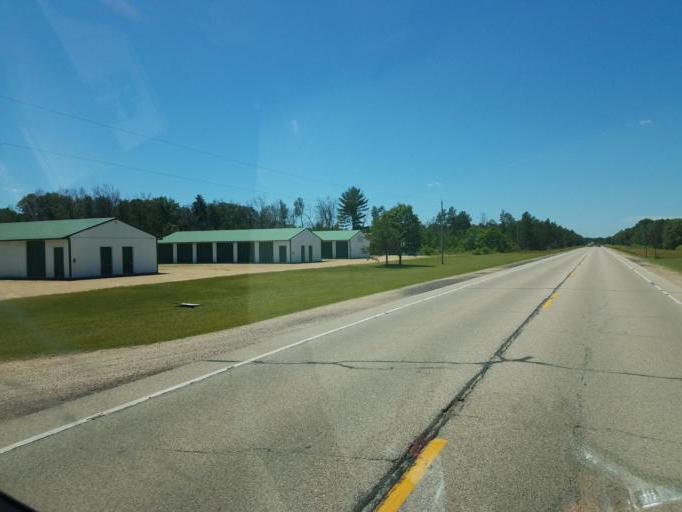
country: US
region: Wisconsin
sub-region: Juneau County
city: New Lisbon
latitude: 44.0367
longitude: -90.0381
